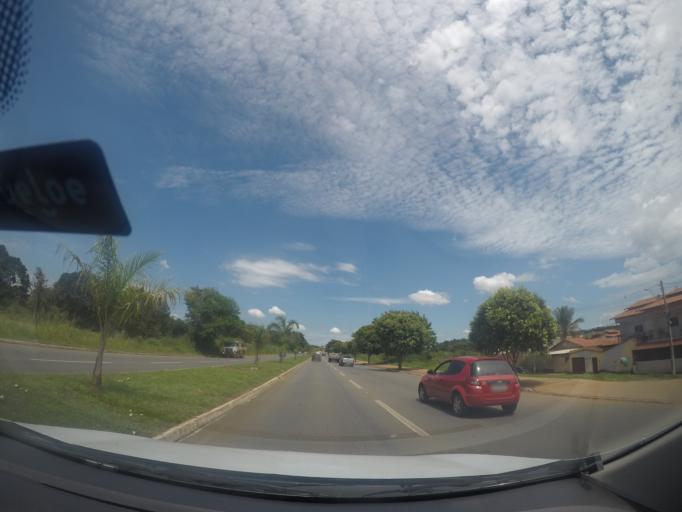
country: BR
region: Goias
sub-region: Goiania
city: Goiania
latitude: -16.6833
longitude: -49.3362
